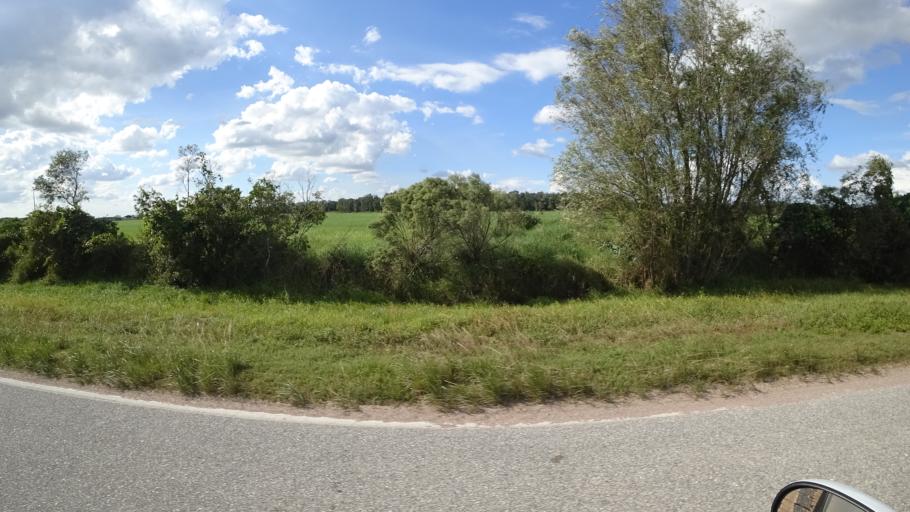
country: US
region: Florida
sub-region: DeSoto County
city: Arcadia
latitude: 27.3110
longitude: -82.1117
